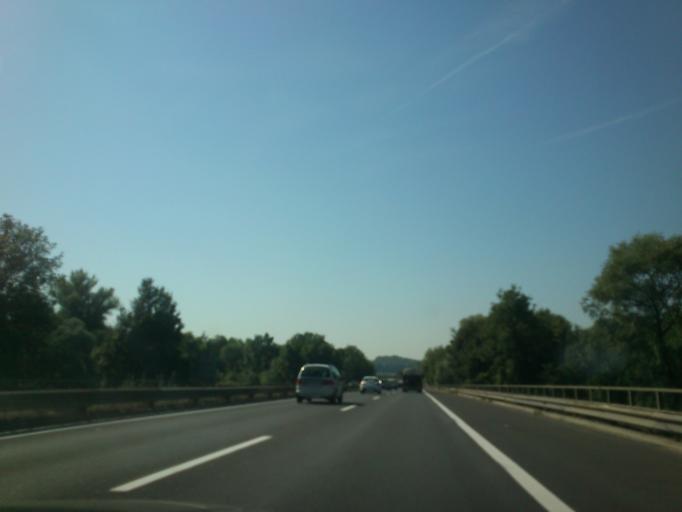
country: AT
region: Upper Austria
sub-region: Politischer Bezirk Linz-Land
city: Ansfelden
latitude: 48.2344
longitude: 14.2977
